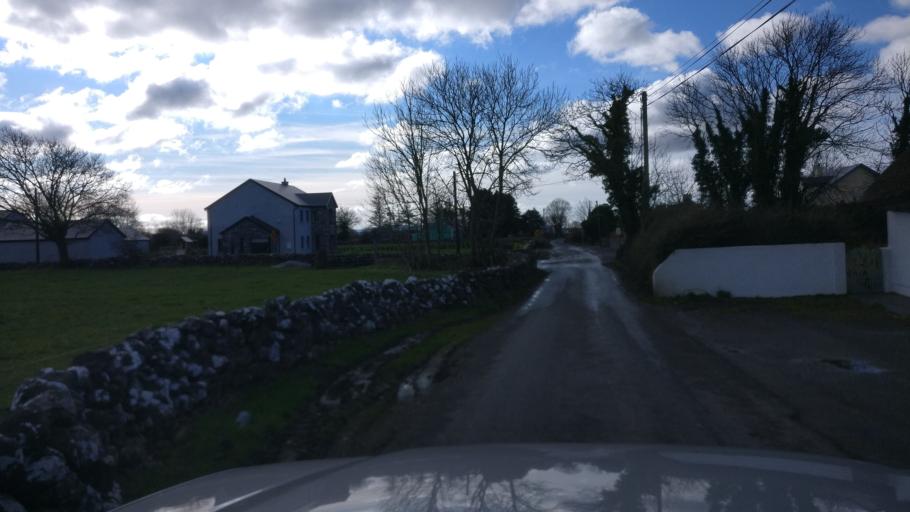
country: IE
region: Connaught
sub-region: County Galway
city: Oranmore
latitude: 53.2828
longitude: -8.8952
